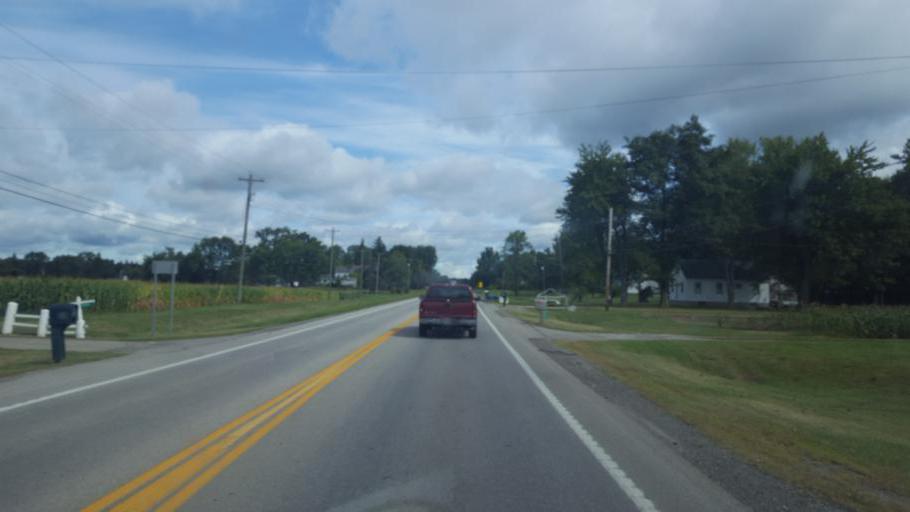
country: US
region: Ohio
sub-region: Lorain County
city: Wellington
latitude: 41.1854
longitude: -82.2171
